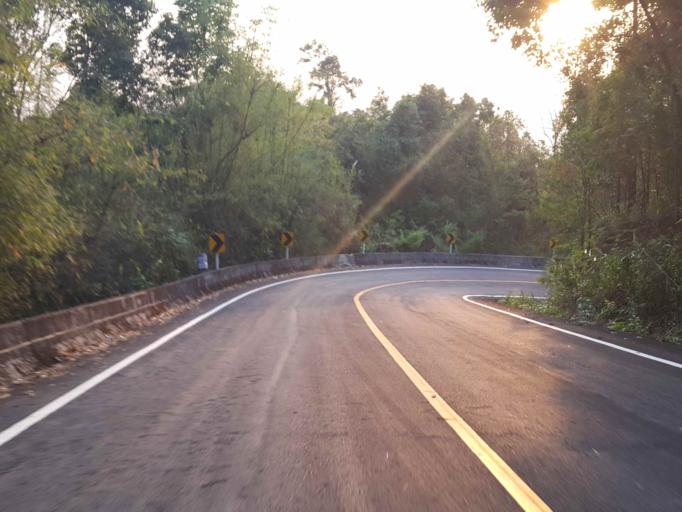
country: TH
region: Chiang Mai
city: Mae On
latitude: 19.0060
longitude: 99.3157
